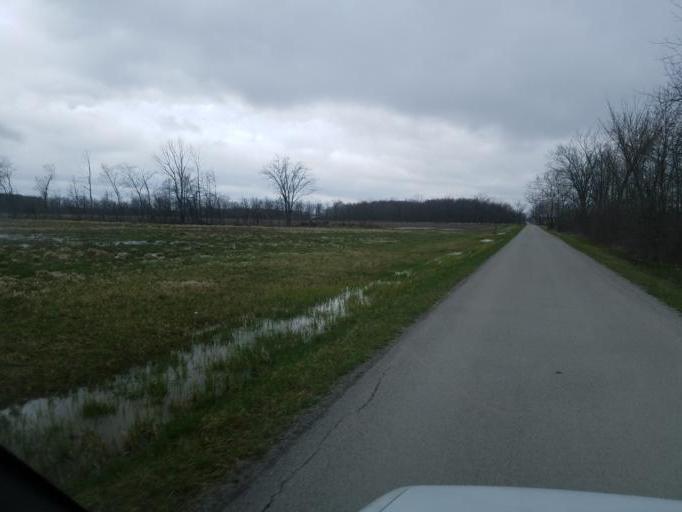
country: US
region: Ohio
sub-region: Wyandot County
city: Upper Sandusky
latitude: 40.6874
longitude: -83.3323
